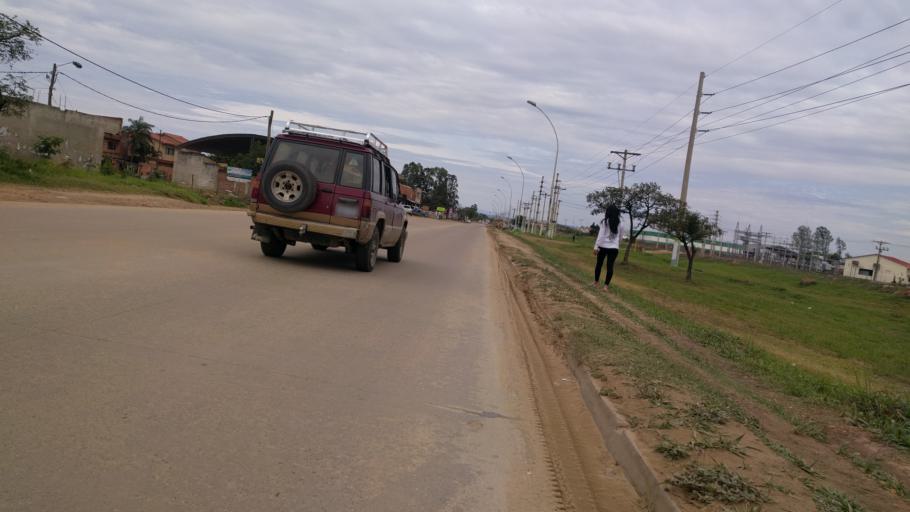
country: BO
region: Santa Cruz
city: Santa Cruz de la Sierra
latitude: -17.8473
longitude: -63.1768
